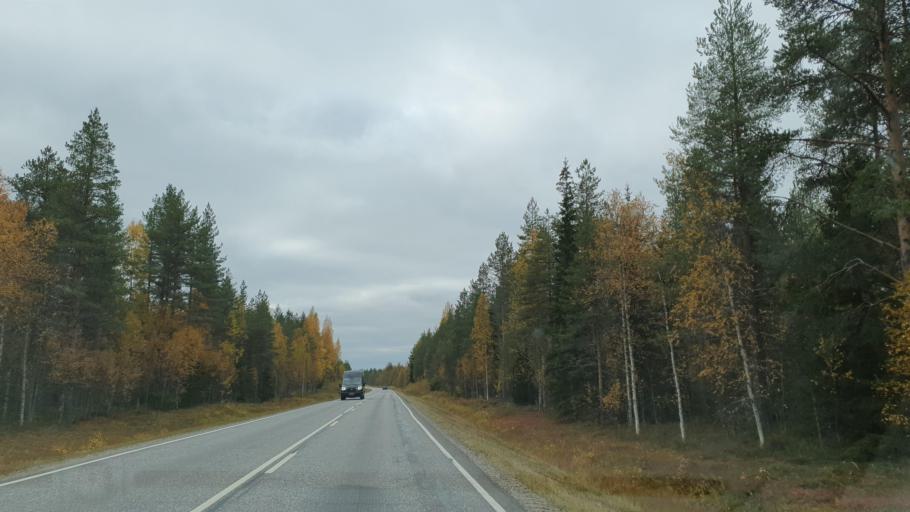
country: FI
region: Lapland
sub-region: Rovaniemi
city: Ranua
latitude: 66.0331
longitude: 26.3322
